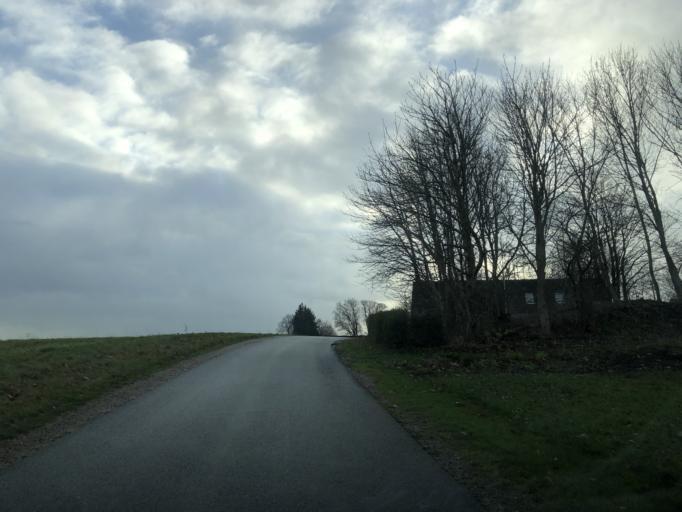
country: DK
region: North Denmark
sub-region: Rebild Kommune
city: Stovring
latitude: 56.8990
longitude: 9.7818
